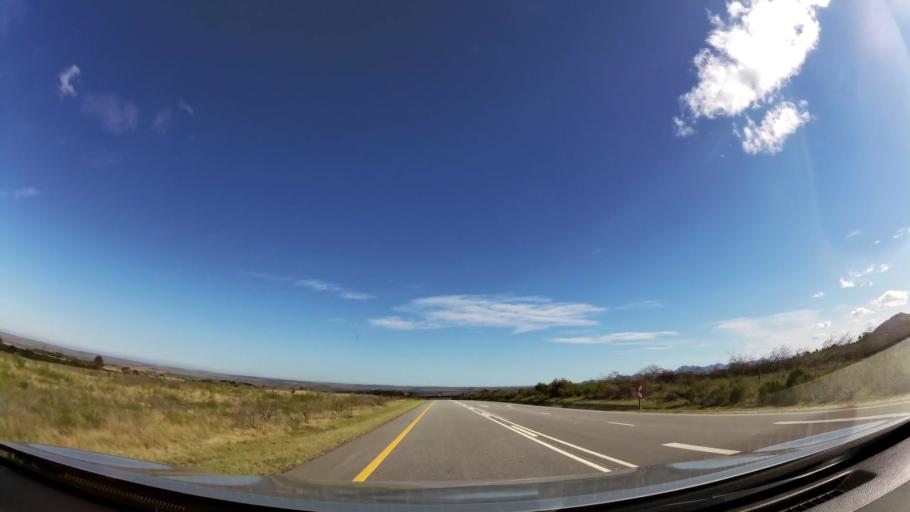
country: ZA
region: Eastern Cape
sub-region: Cacadu District Municipality
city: Kruisfontein
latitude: -33.9992
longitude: 24.6856
